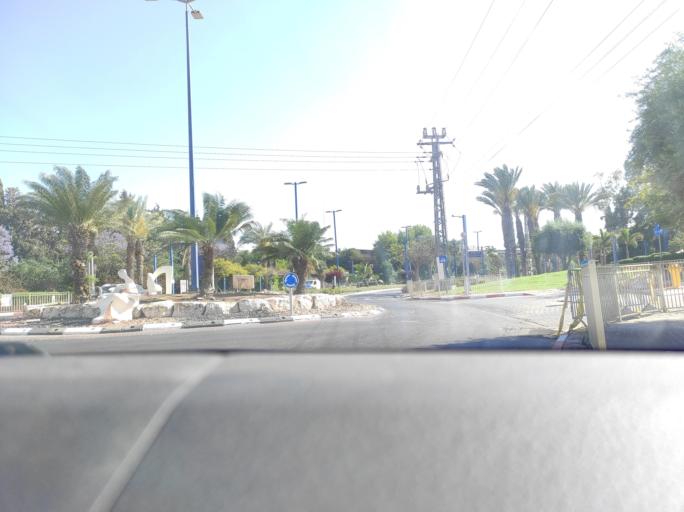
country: IL
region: Southern District
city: Sederot
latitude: 31.5201
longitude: 34.5930
